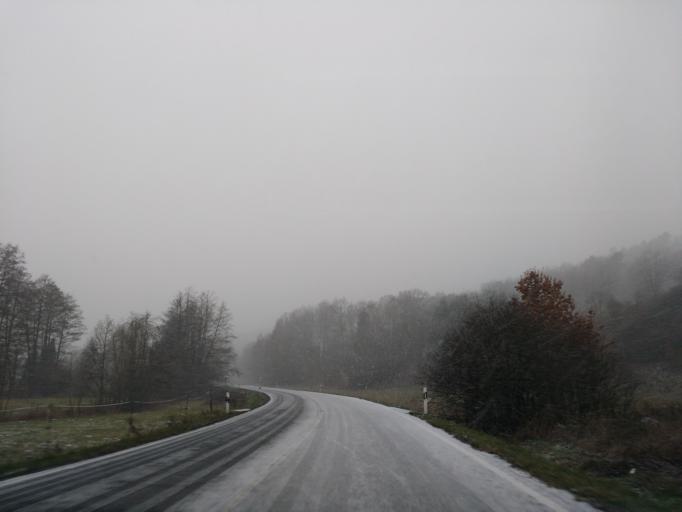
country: DE
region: Hesse
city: Spangenberg
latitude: 51.1138
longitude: 9.6099
